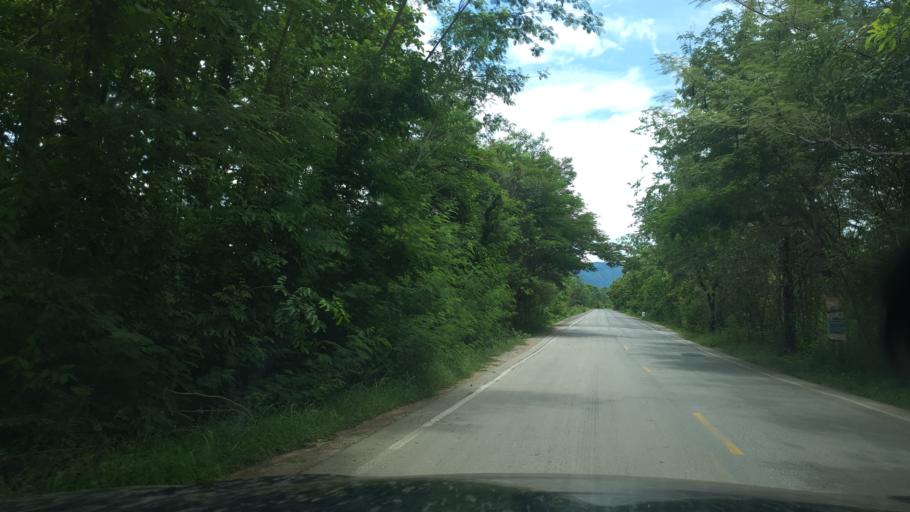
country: TH
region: Lampang
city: Sop Prap
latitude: 17.9251
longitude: 99.3804
